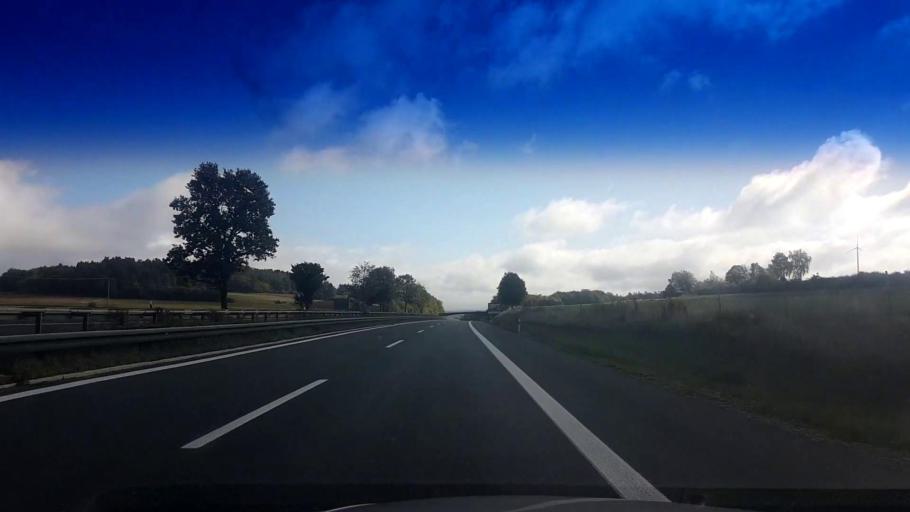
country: DE
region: Bavaria
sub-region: Upper Franconia
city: Kasendorf
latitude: 50.0095
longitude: 11.3500
